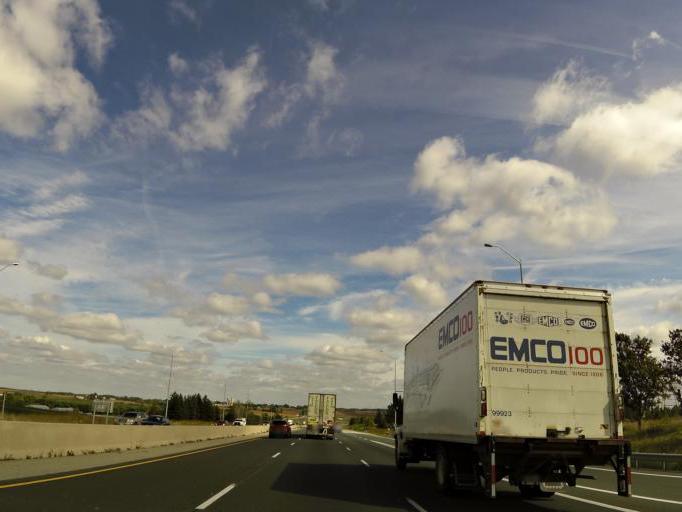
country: CA
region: Ontario
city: Ingersoll
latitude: 42.9739
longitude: -80.9629
